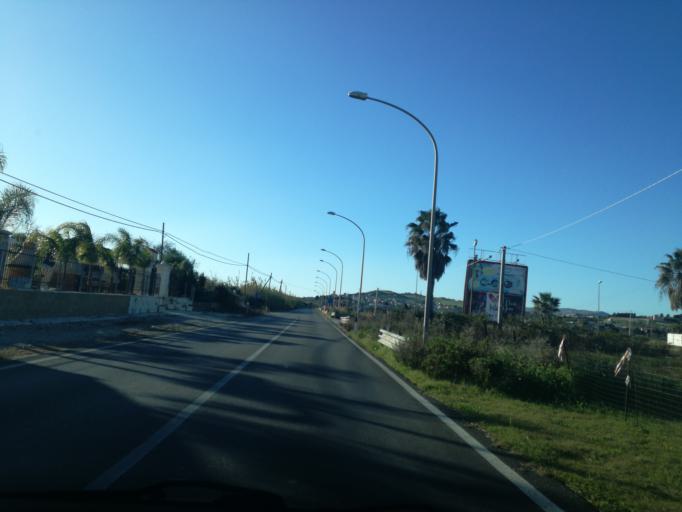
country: IT
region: Sicily
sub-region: Provincia di Caltanissetta
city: Gela
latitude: 37.0965
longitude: 14.1697
